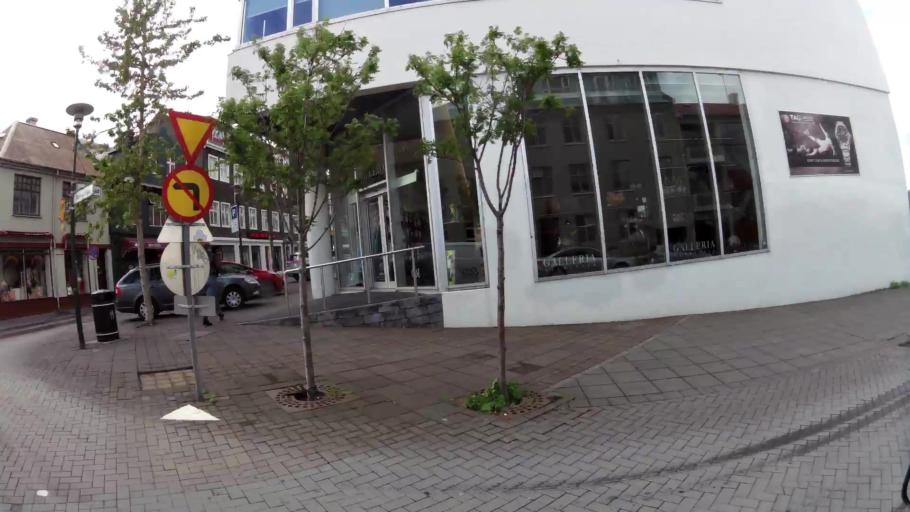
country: IS
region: Capital Region
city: Reykjavik
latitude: 64.1438
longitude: -21.9191
